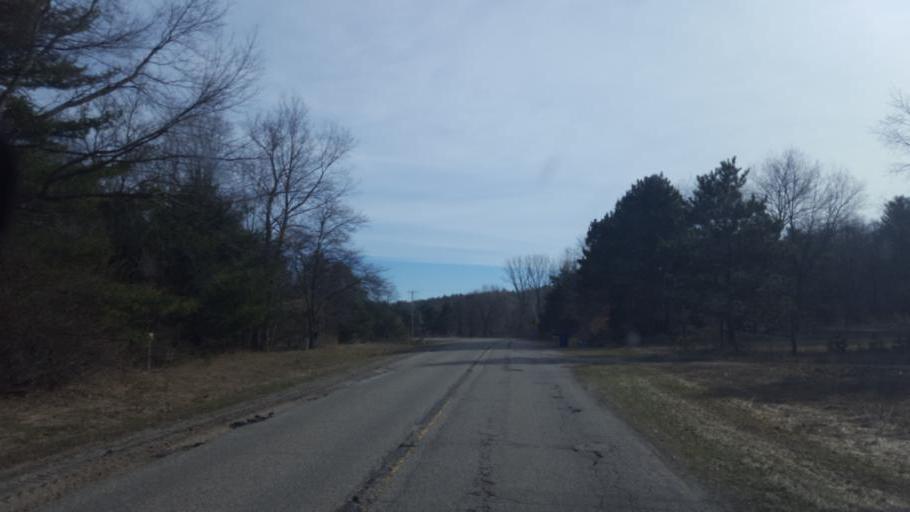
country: US
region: Michigan
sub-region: Mecosta County
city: Big Rapids
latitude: 43.5653
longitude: -85.5134
